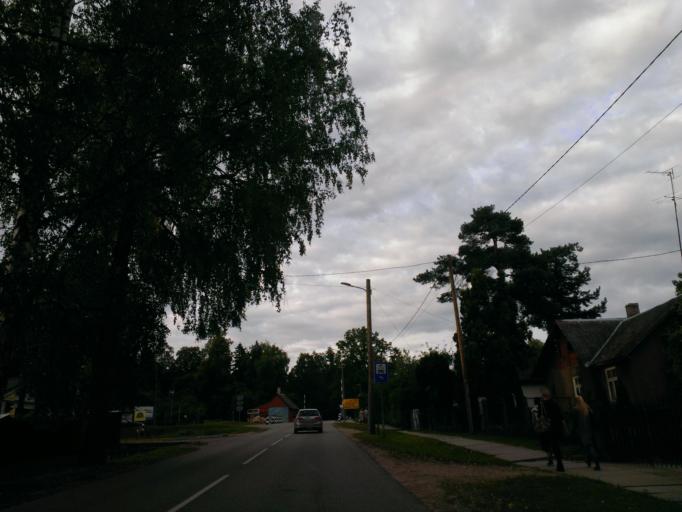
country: LV
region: Ogre
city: Ogre
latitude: 56.8209
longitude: 24.5815
